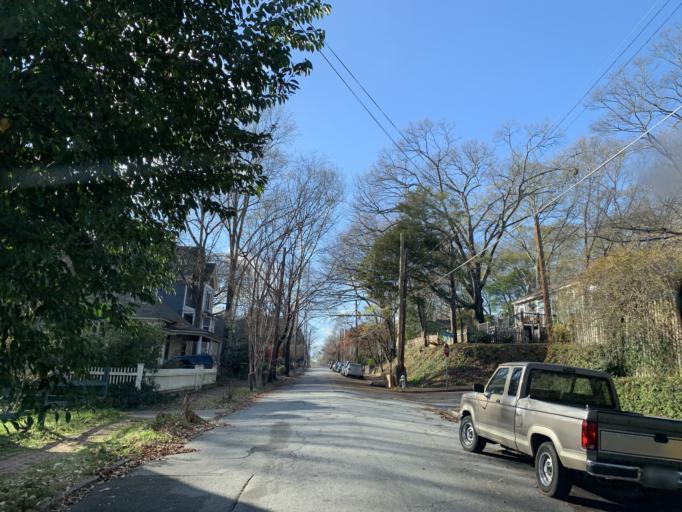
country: US
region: Georgia
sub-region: Fulton County
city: Atlanta
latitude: 33.7378
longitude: -84.3746
